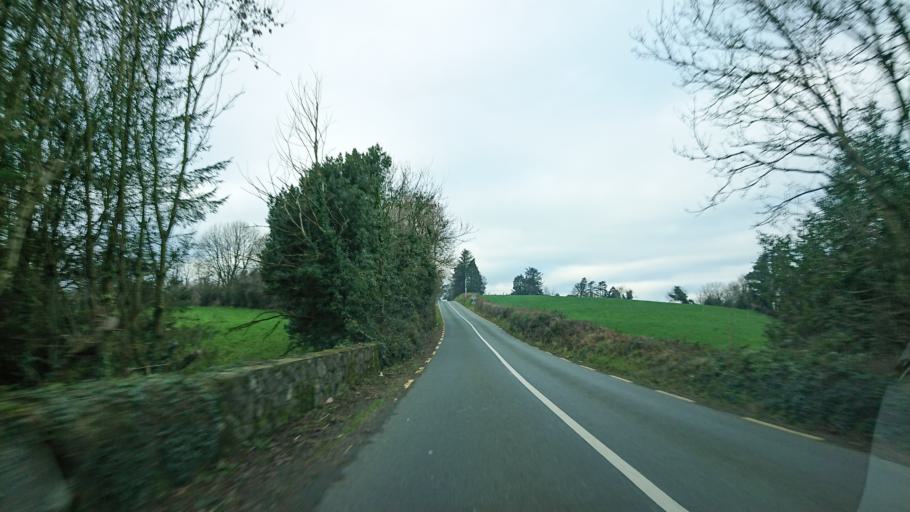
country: IE
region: Munster
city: Carrick-on-Suir
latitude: 52.3007
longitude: -7.4805
